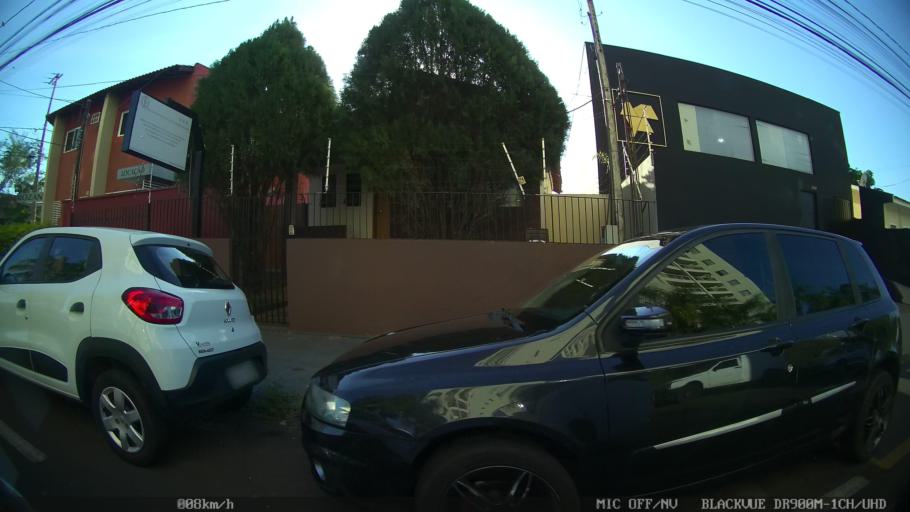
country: BR
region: Sao Paulo
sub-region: Sao Jose Do Rio Preto
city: Sao Jose do Rio Preto
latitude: -20.8147
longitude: -49.3938
